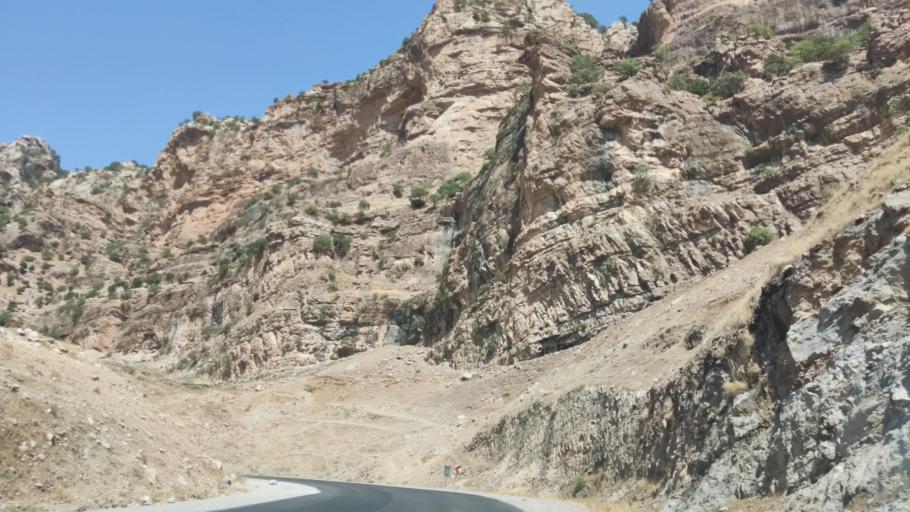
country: IQ
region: Arbil
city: Ruwandiz
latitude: 36.6326
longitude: 44.4464
